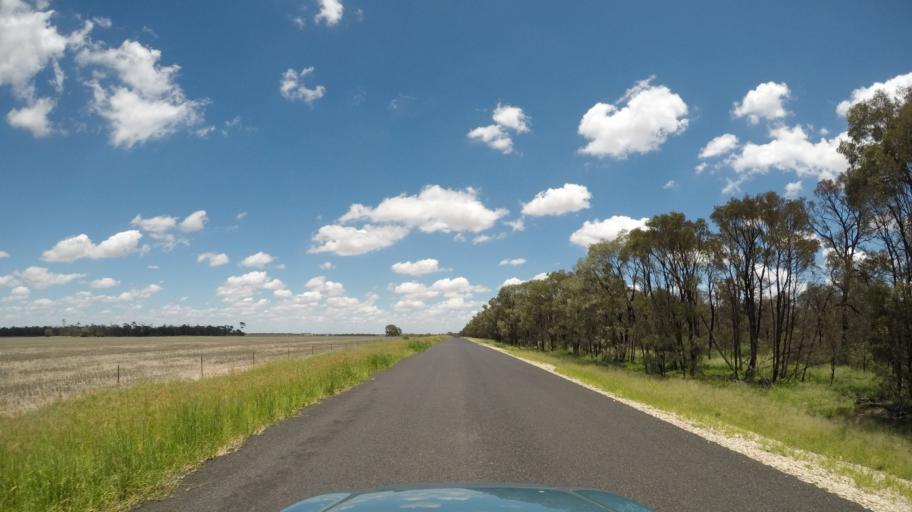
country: AU
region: Queensland
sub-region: Goondiwindi
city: Goondiwindi
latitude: -28.1589
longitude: 150.3946
